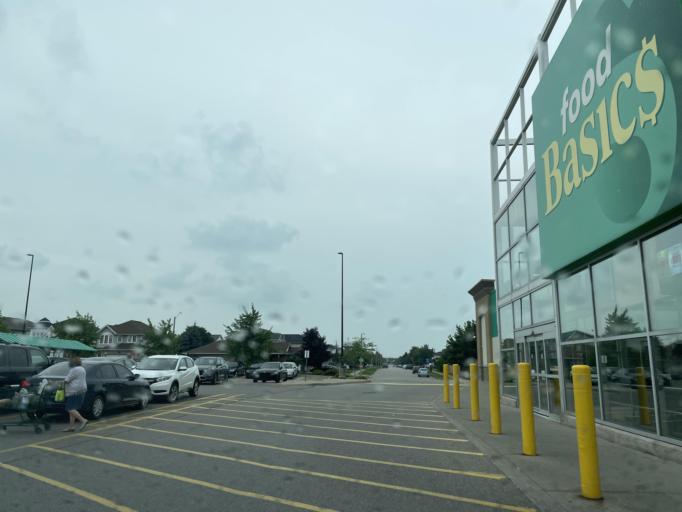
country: CA
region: Ontario
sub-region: Wellington County
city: Guelph
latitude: 43.5000
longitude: -80.1915
